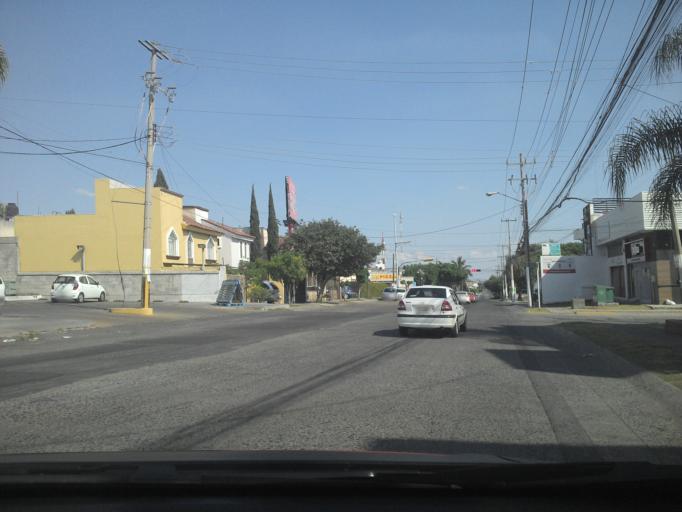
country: MX
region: Jalisco
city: Guadalajara
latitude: 20.6415
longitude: -103.4340
